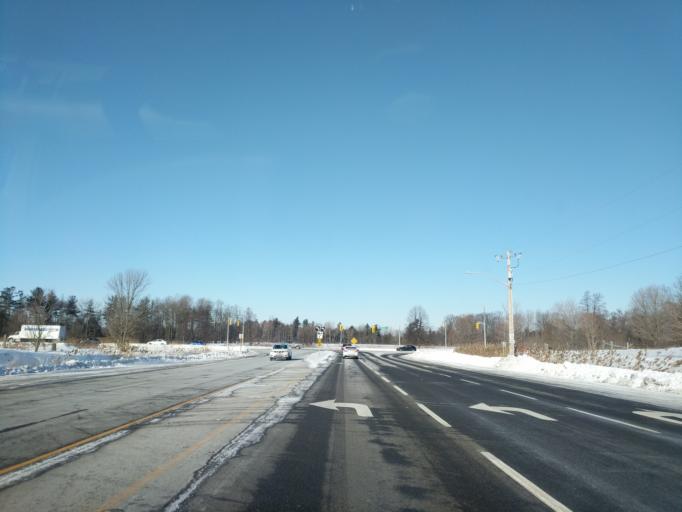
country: CA
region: Ontario
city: Pickering
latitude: 43.8690
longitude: -79.1394
